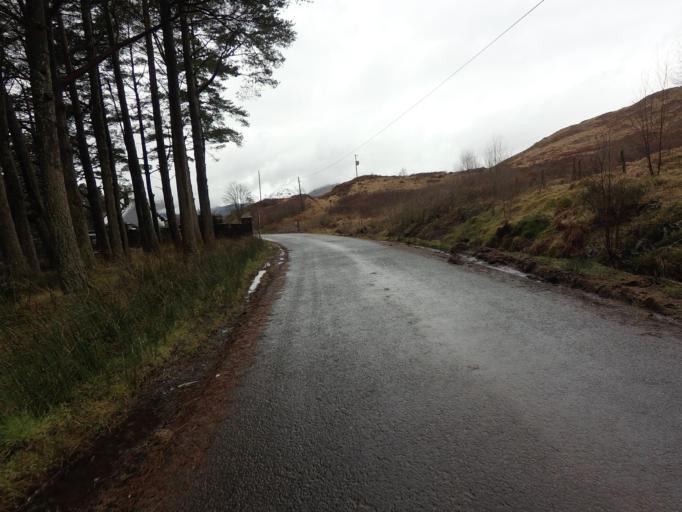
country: GB
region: Scotland
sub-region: Argyll and Bute
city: Garelochhead
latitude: 56.2498
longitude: -4.6541
